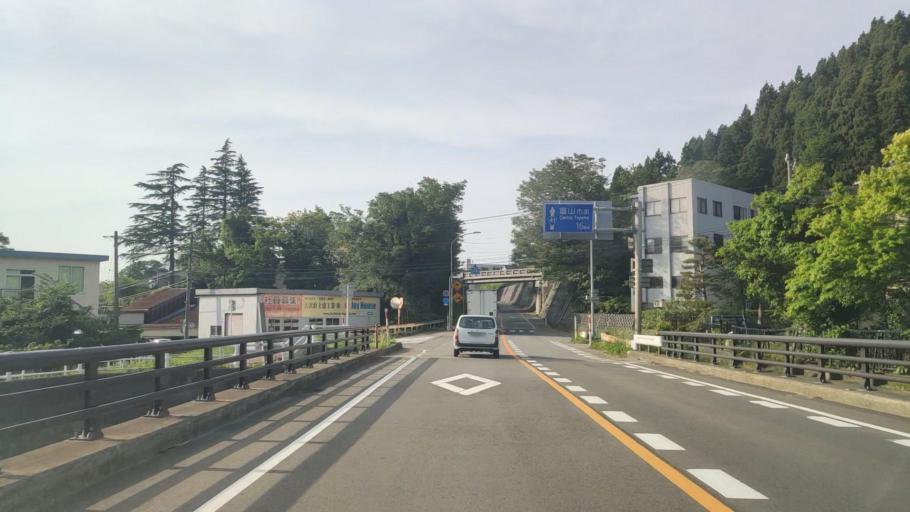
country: JP
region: Toyama
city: Yatsuomachi-higashikumisaka
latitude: 36.5578
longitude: 137.2156
